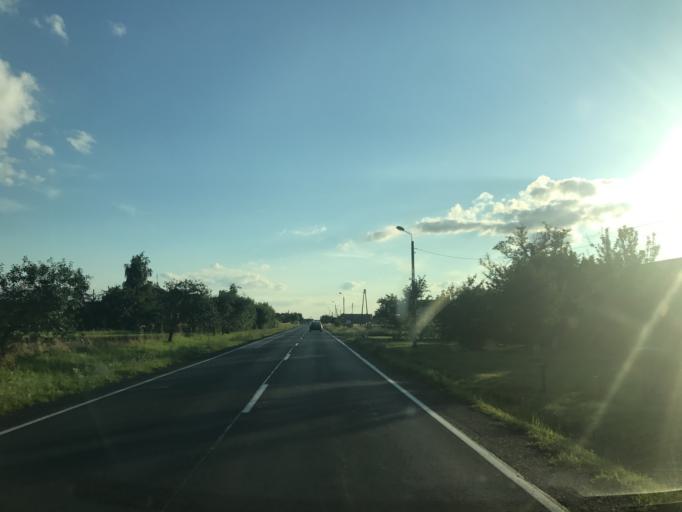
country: PL
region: Greater Poland Voivodeship
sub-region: Powiat jarocinski
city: Jaraczewo
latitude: 51.9705
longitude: 17.3356
